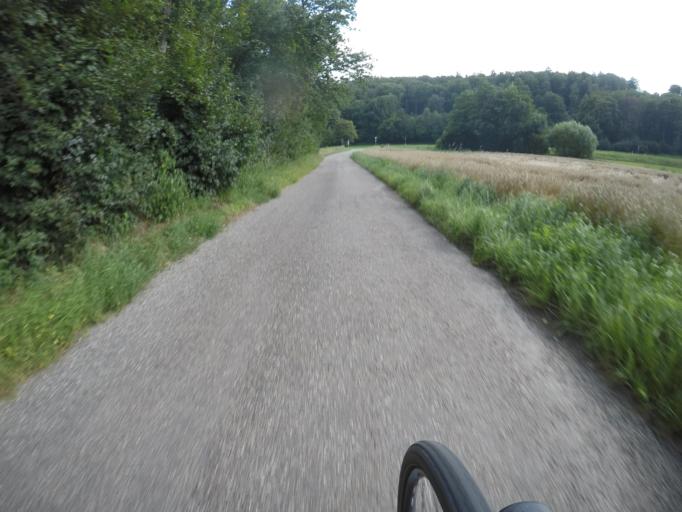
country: DE
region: Baden-Wuerttemberg
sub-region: Karlsruhe Region
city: Niefern-Oschelbronn
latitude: 48.9387
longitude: 8.7766
